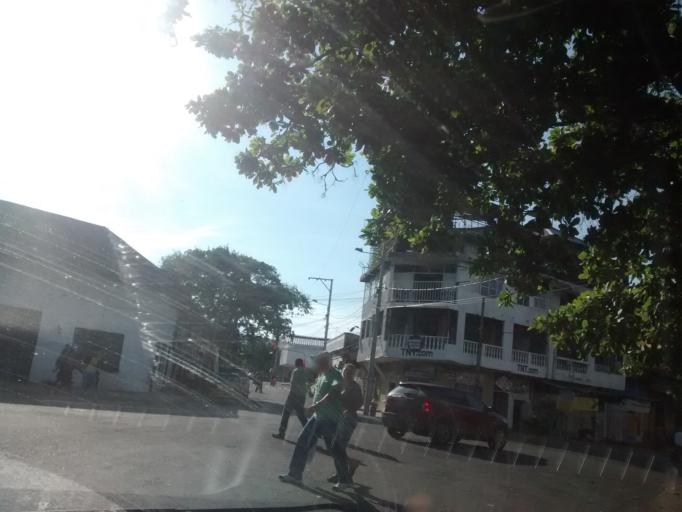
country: CO
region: Cundinamarca
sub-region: Girardot
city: Girardot City
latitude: 4.2965
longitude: -74.8045
